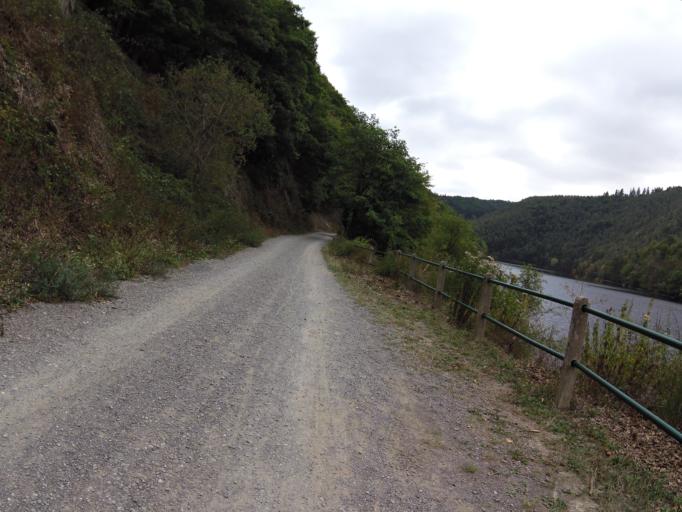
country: DE
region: North Rhine-Westphalia
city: Heimbach
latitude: 50.6064
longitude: 6.4083
